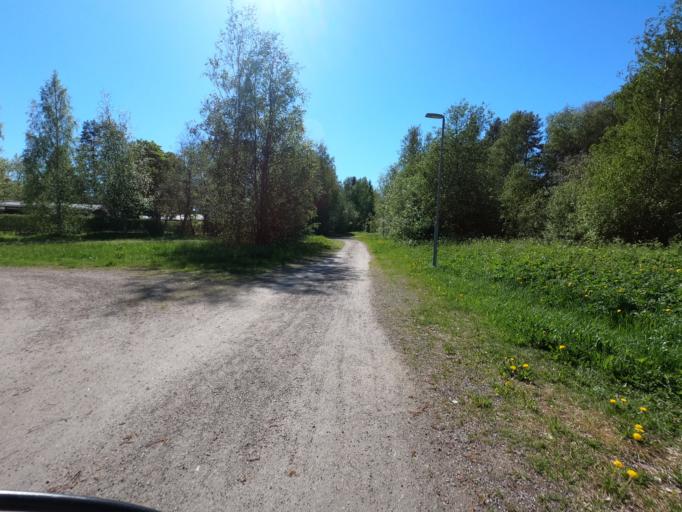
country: FI
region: North Karelia
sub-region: Joensuu
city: Joensuu
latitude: 62.5882
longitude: 29.7991
